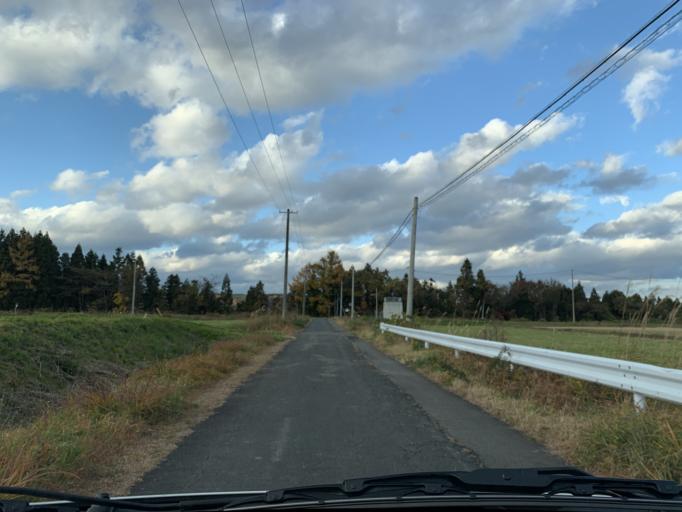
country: JP
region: Iwate
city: Mizusawa
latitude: 39.1153
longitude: 141.0232
